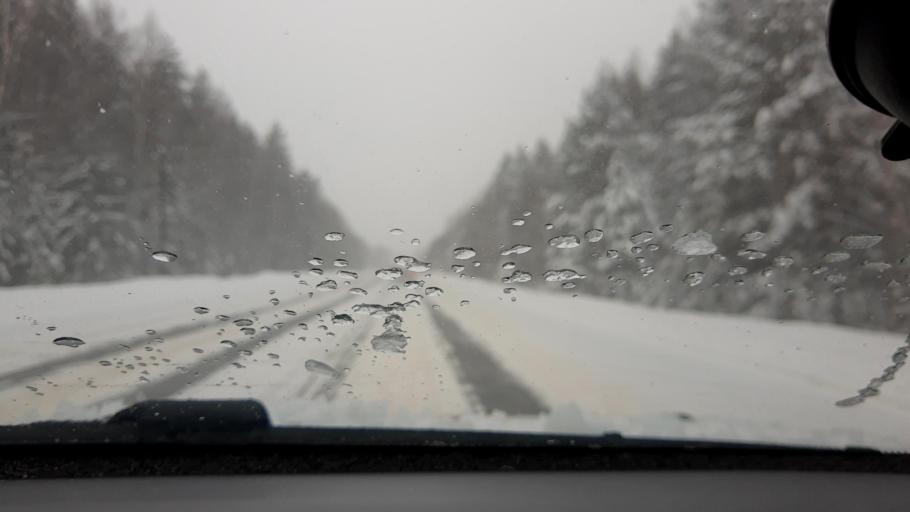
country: RU
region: Nizjnij Novgorod
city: Purekh
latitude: 56.6317
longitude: 43.1740
